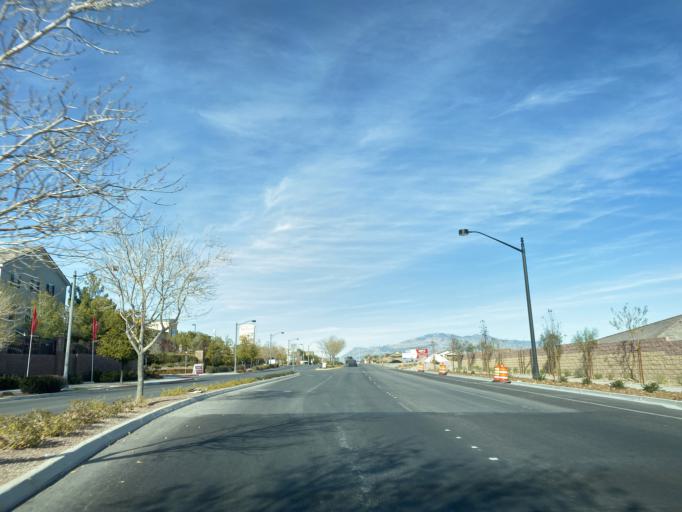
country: US
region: Nevada
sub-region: Clark County
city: Summerlin South
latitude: 36.2896
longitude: -115.3148
